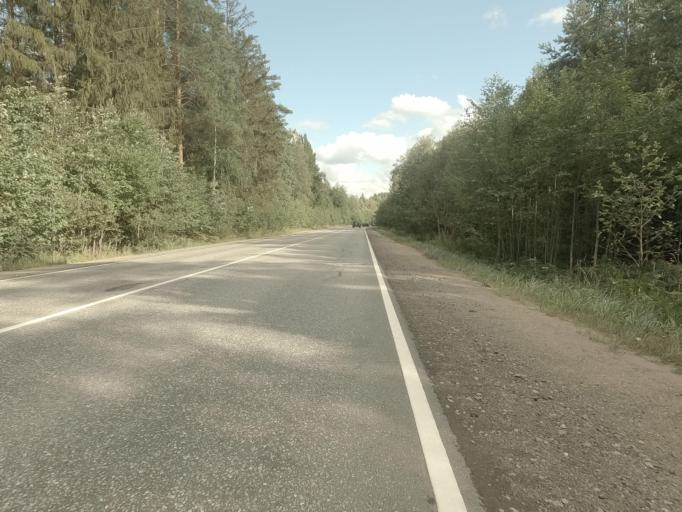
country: RU
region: Leningrad
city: Shcheglovo
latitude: 60.0089
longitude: 30.8592
